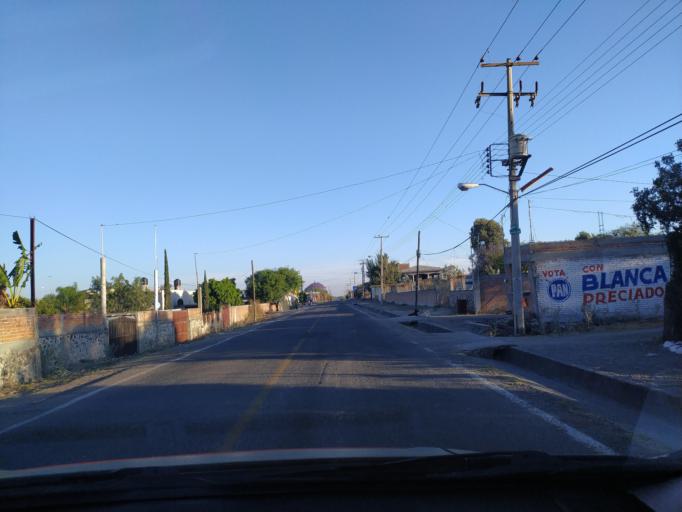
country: MX
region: Guanajuato
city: Ciudad Manuel Doblado
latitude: 20.7481
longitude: -101.8243
